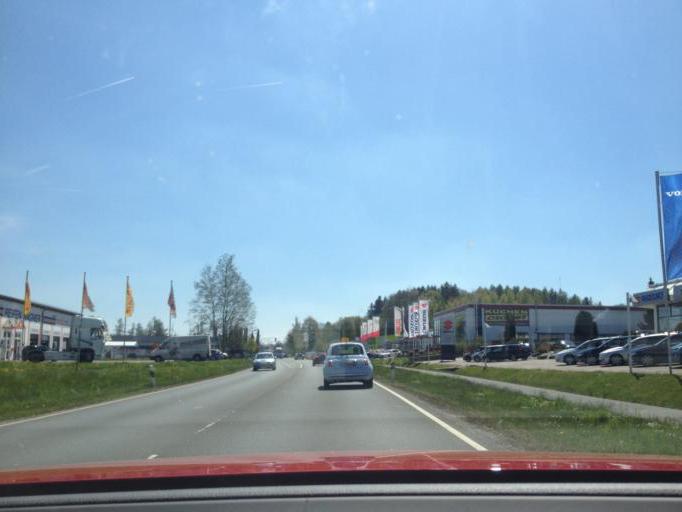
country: DE
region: Bavaria
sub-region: Upper Franconia
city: Oberkotzau
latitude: 50.2753
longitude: 11.9246
